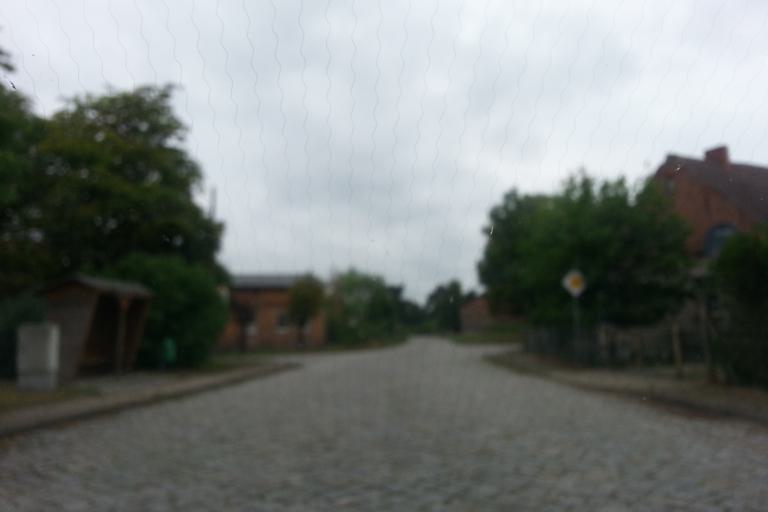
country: DE
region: Mecklenburg-Vorpommern
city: Ferdinandshof
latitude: 53.6875
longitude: 13.9002
